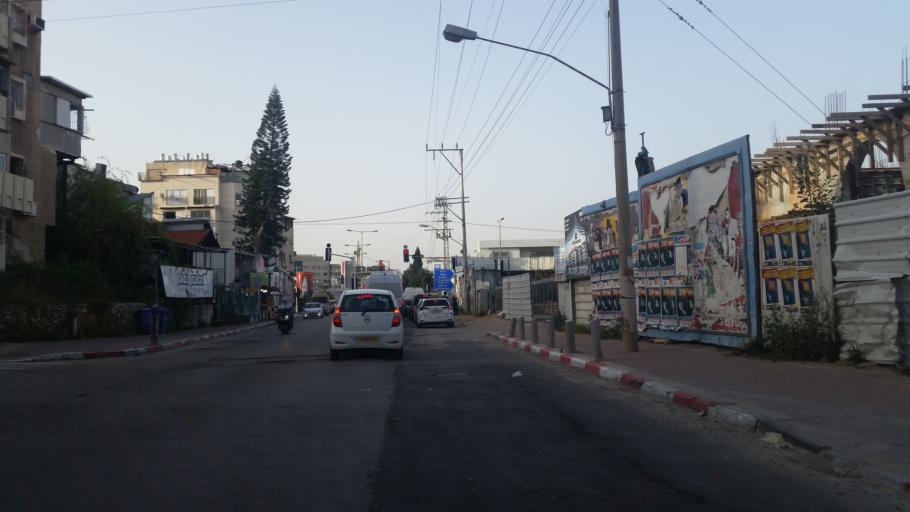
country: IL
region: Tel Aviv
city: Giv`at Shemu'el
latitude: 32.0751
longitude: 34.8425
